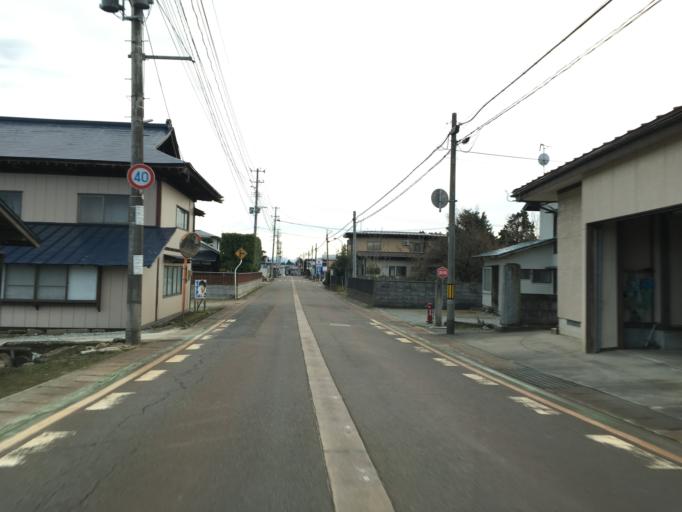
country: JP
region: Yamagata
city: Nagai
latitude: 38.1765
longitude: 140.0644
